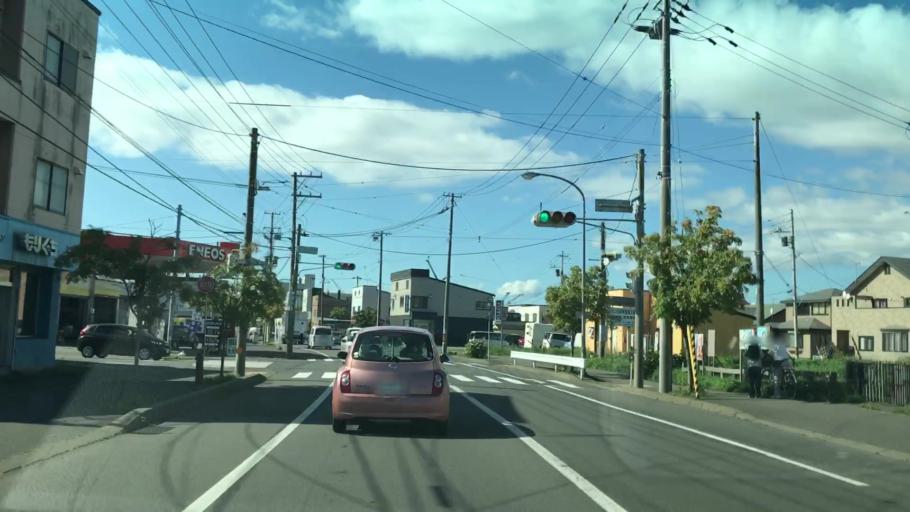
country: JP
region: Hokkaido
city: Muroran
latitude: 42.3333
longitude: 140.9624
